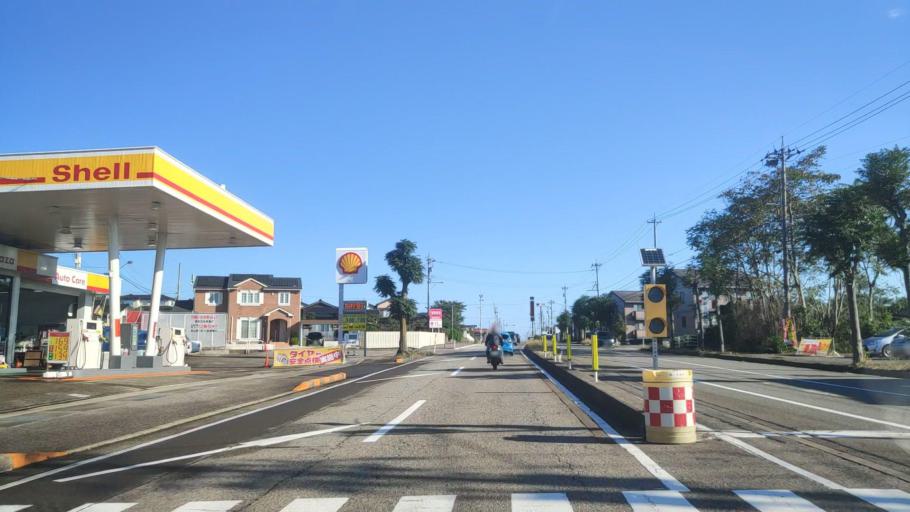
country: JP
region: Ishikawa
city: Tsubata
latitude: 36.7238
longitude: 136.6984
